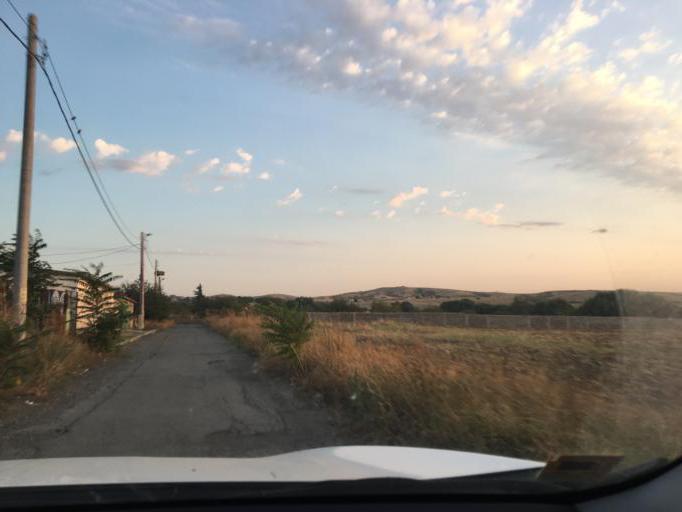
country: BG
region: Burgas
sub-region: Obshtina Burgas
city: Burgas
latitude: 42.6103
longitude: 27.4975
